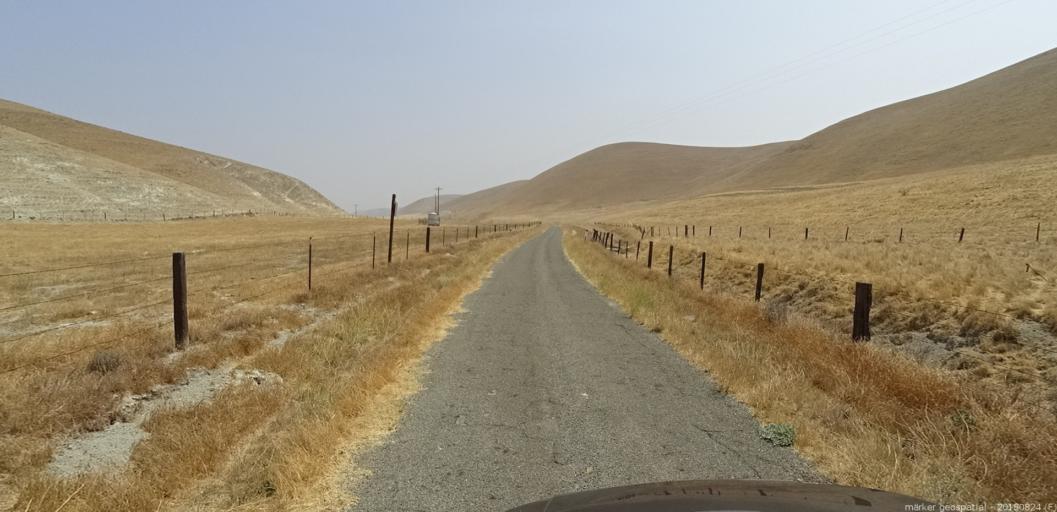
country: US
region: California
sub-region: Monterey County
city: King City
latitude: 36.1914
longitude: -120.9776
